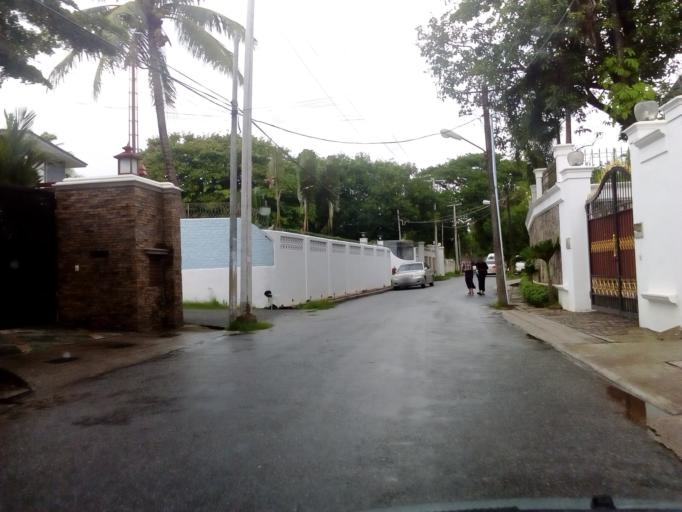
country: MM
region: Yangon
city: Yangon
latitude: 16.8155
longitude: 96.1480
